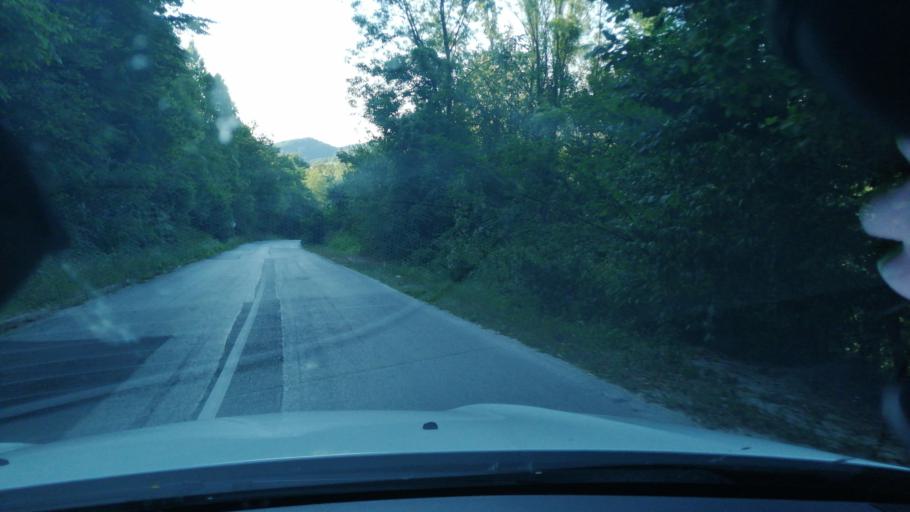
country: RS
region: Central Serbia
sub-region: Moravicki Okrug
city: Ivanjica
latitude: 43.6722
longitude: 20.2639
